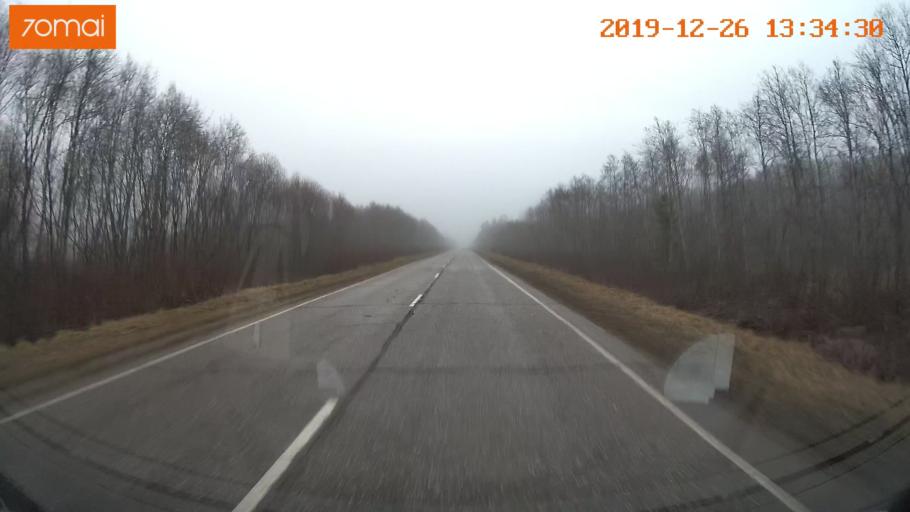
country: RU
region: Vologda
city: Sheksna
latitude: 58.8050
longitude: 38.3247
